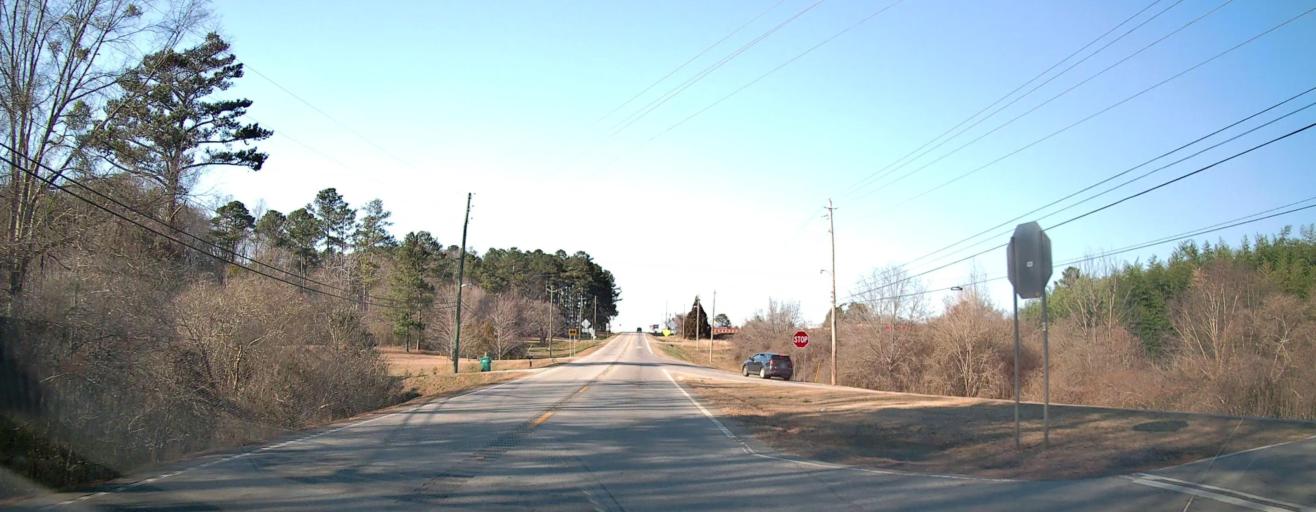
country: US
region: Georgia
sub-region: Butts County
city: Jackson
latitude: 33.3043
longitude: -83.9801
